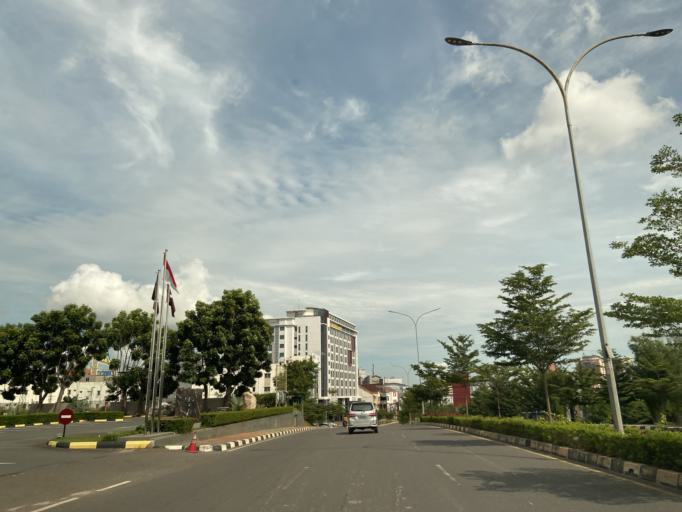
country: SG
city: Singapore
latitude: 1.1475
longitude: 104.0150
